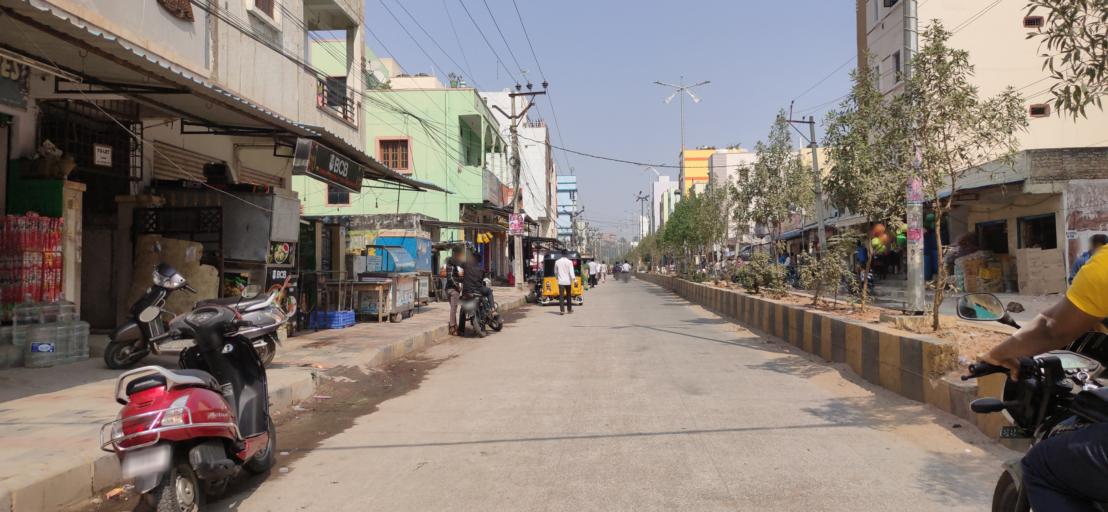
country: IN
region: Telangana
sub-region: Rangareddi
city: Kukatpalli
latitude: 17.5098
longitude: 78.4072
